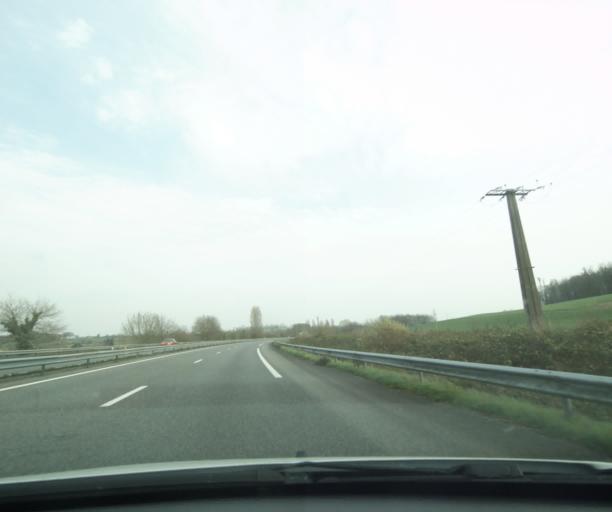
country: FR
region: Aquitaine
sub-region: Departement des Pyrenees-Atlantiques
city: Puyoo
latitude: 43.5081
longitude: -0.8449
